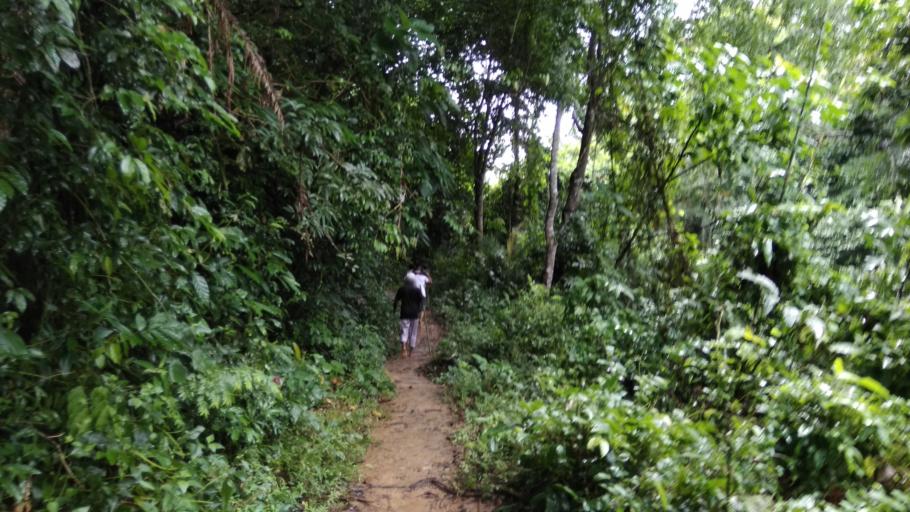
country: IN
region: Tripura
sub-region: Dhalai
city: Kamalpur
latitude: 24.1731
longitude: 91.8873
